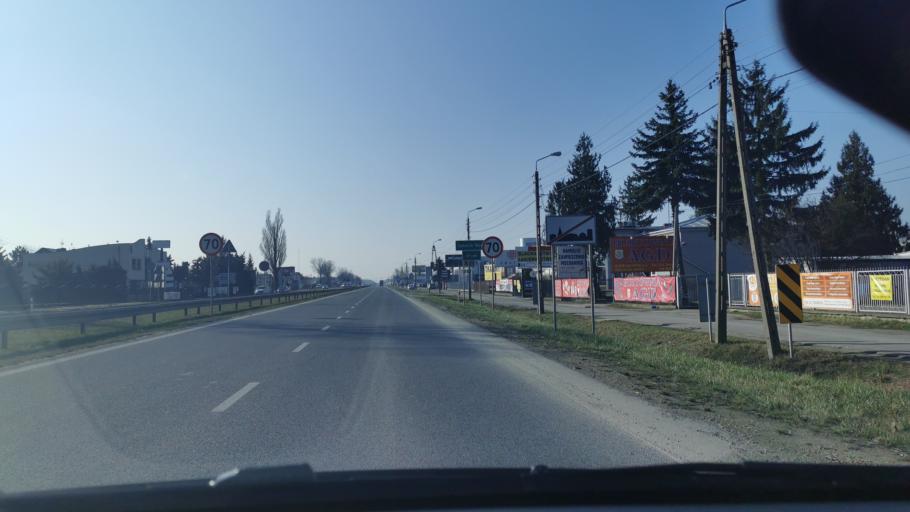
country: PL
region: Masovian Voivodeship
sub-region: Powiat pruszkowski
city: Nowe Grocholice
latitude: 52.1237
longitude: 20.8945
